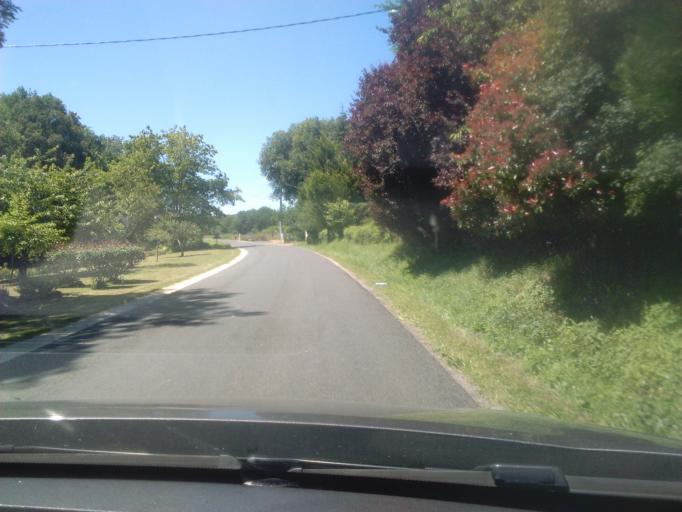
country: FR
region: Centre
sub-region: Departement du Loir-et-Cher
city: Saint-Sulpice-de-Pommeray
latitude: 47.6044
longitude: 1.2259
